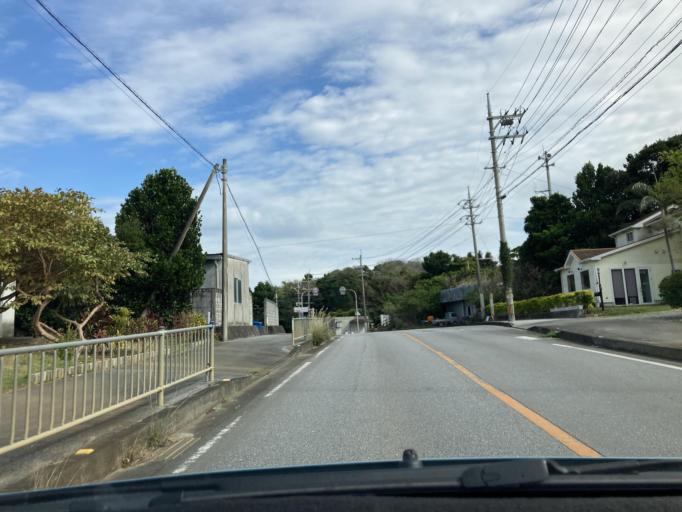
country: JP
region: Okinawa
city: Nago
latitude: 26.6965
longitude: 127.9433
